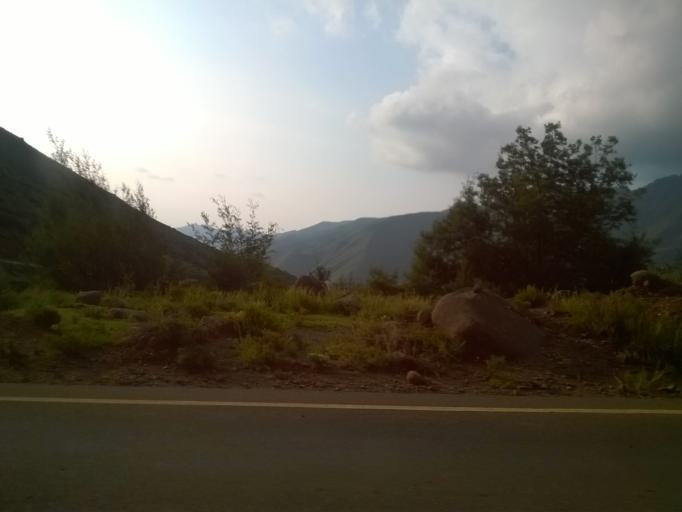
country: LS
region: Butha-Buthe
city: Butha-Buthe
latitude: -29.0601
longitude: 28.3570
